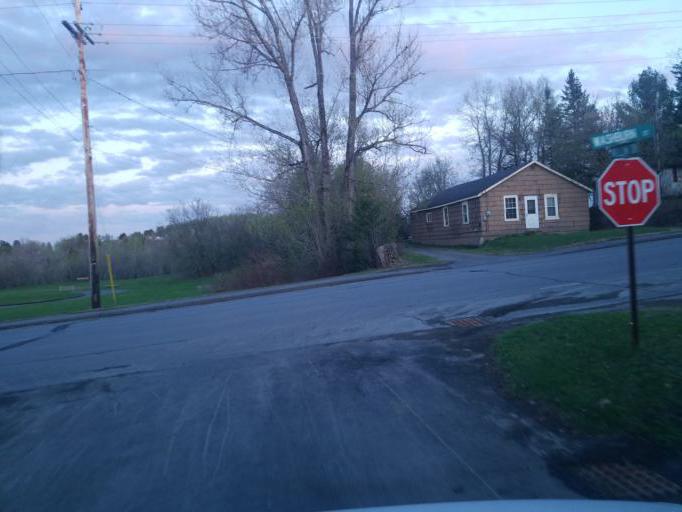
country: US
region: Maine
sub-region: Aroostook County
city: Caribou
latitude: 46.8575
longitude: -68.0225
